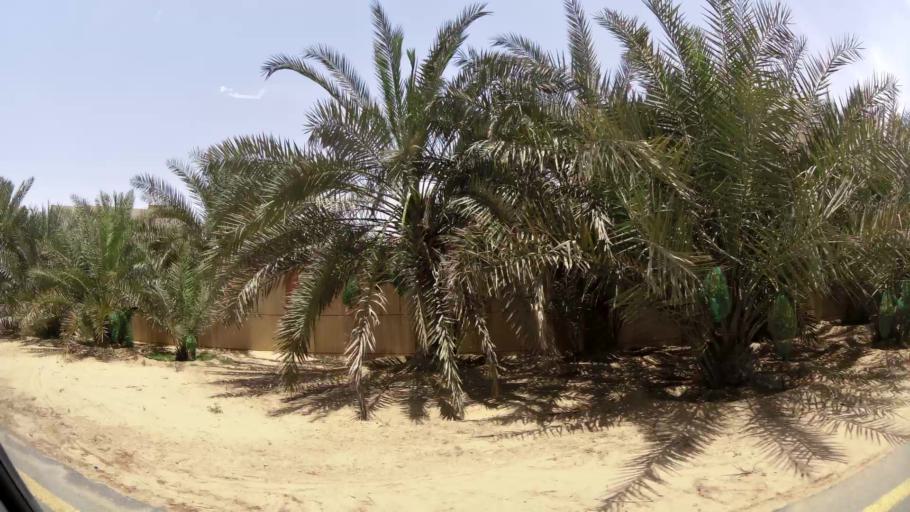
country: AE
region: Ash Shariqah
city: Sharjah
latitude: 25.2341
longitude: 55.4561
